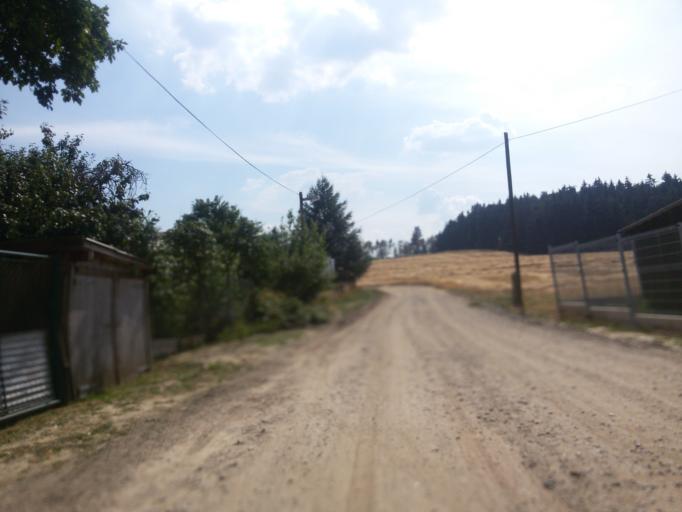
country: CZ
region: South Moravian
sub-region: Okres Blansko
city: Kunstat
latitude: 49.4625
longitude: 16.4615
